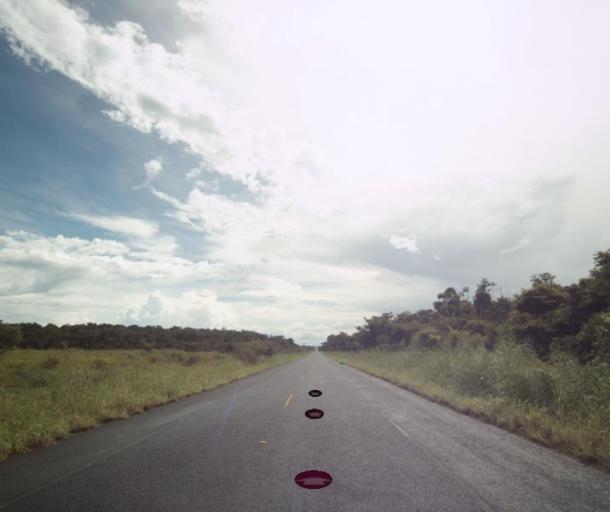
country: BR
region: Goias
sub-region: Sao Miguel Do Araguaia
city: Sao Miguel do Araguaia
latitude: -13.2998
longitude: -50.3084
